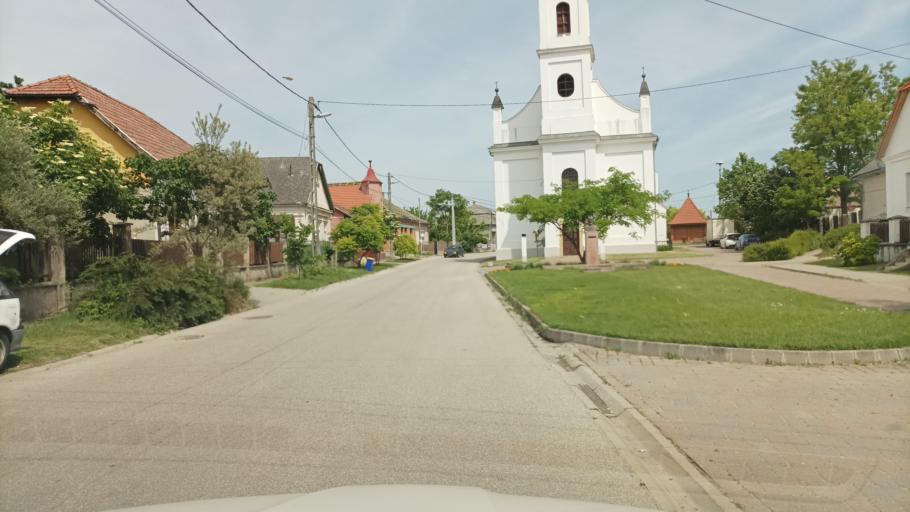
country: HU
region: Fejer
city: Adony
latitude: 47.0892
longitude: 18.9255
